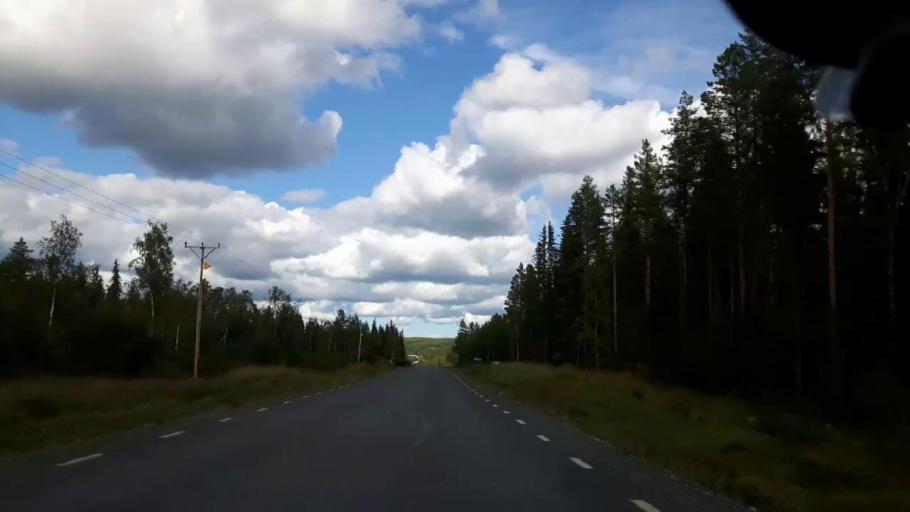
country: SE
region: Jaemtland
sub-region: Braecke Kommun
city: Braecke
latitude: 63.2854
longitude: 15.5839
